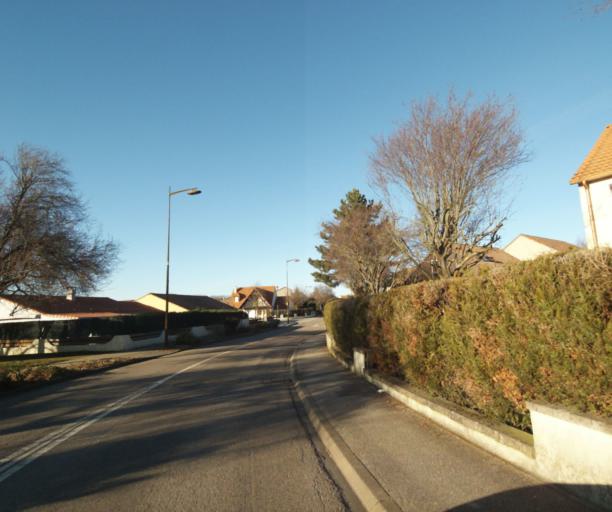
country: FR
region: Lorraine
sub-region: Departement de Meurthe-et-Moselle
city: Pulnoy
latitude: 48.7054
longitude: 6.2570
